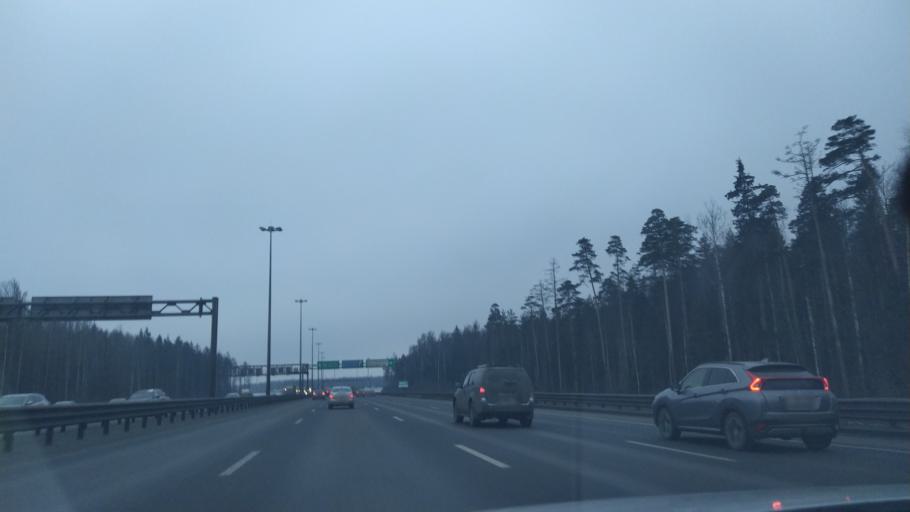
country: RU
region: Leningrad
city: Yanino Vtoroye
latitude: 59.9532
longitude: 30.5472
